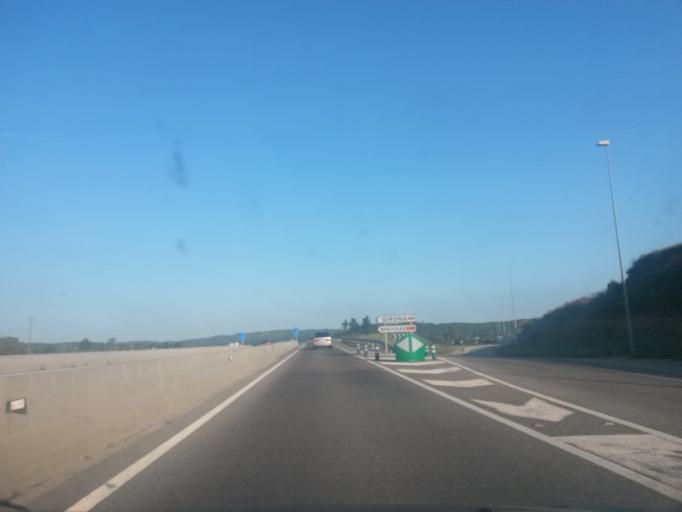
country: ES
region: Catalonia
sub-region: Provincia de Girona
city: Besalu
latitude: 42.2051
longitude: 2.7037
